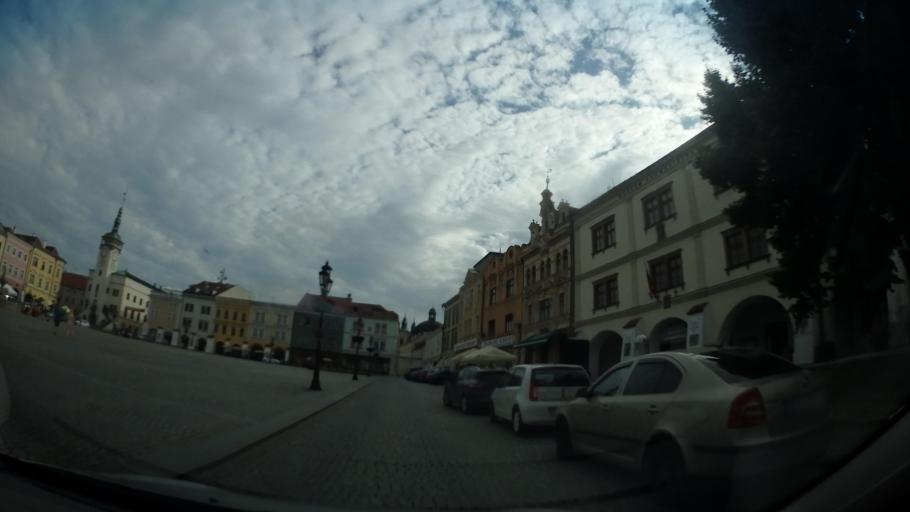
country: CZ
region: Zlin
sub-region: Okres Kromeriz
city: Kromeriz
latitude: 49.2991
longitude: 17.3932
